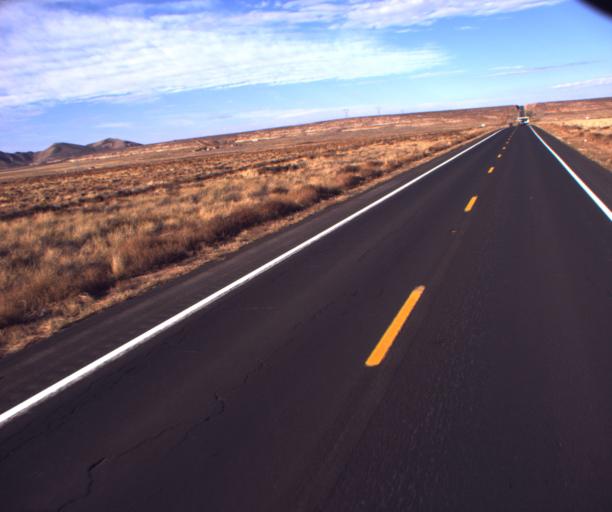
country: US
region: Arizona
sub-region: Apache County
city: Lukachukai
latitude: 36.9623
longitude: -109.4275
